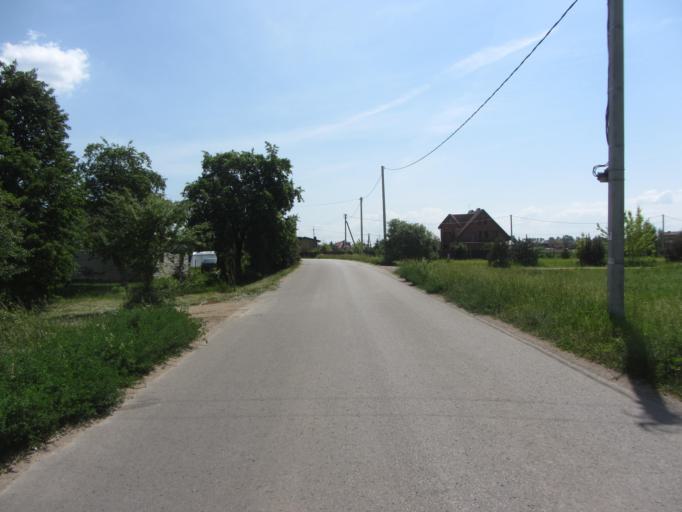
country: LT
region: Kauno apskritis
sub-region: Kauno rajonas
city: Karmelava
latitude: 54.9317
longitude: 24.0878
